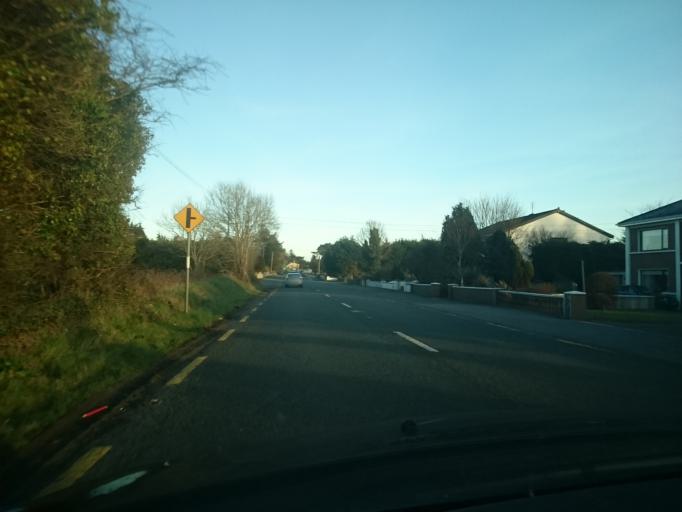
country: IE
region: Connaught
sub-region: Maigh Eo
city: Claremorris
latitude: 53.7400
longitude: -9.0118
